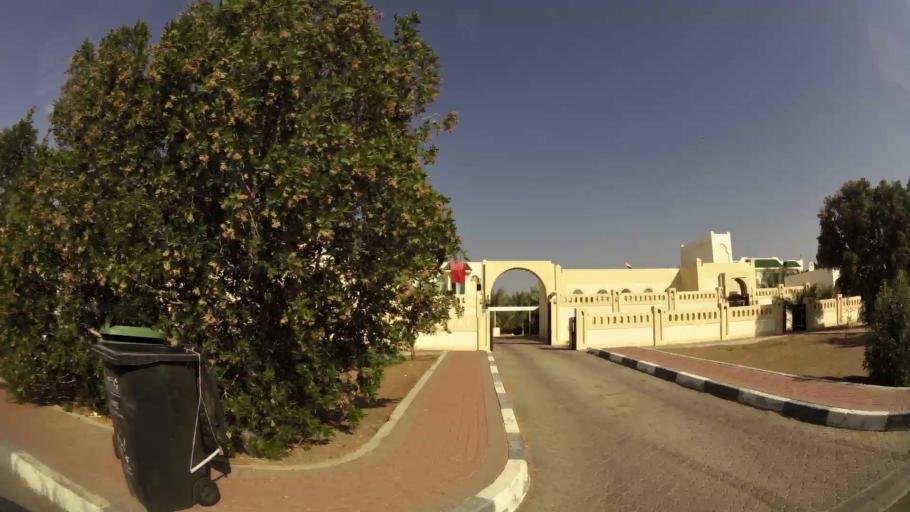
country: AE
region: Abu Dhabi
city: Al Ain
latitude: 24.0737
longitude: 55.8686
